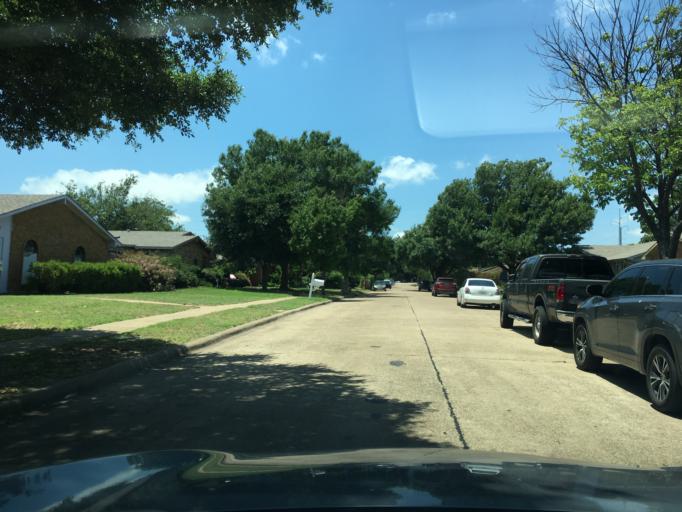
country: US
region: Texas
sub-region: Dallas County
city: Garland
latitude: 32.9539
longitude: -96.6717
